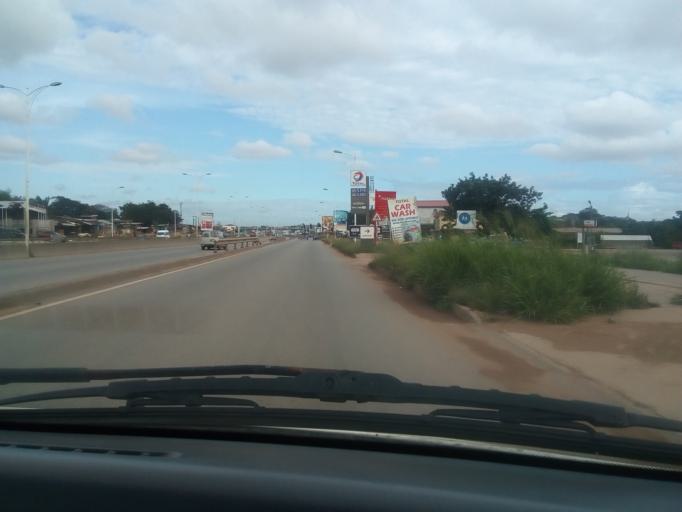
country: GH
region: Greater Accra
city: Dome
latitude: 5.6560
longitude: -0.2631
